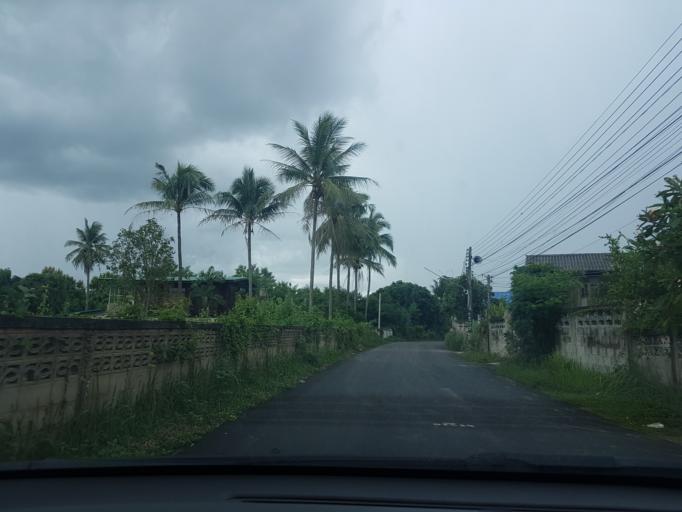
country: TH
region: Lampang
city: Ko Kha
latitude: 18.2257
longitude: 99.4198
